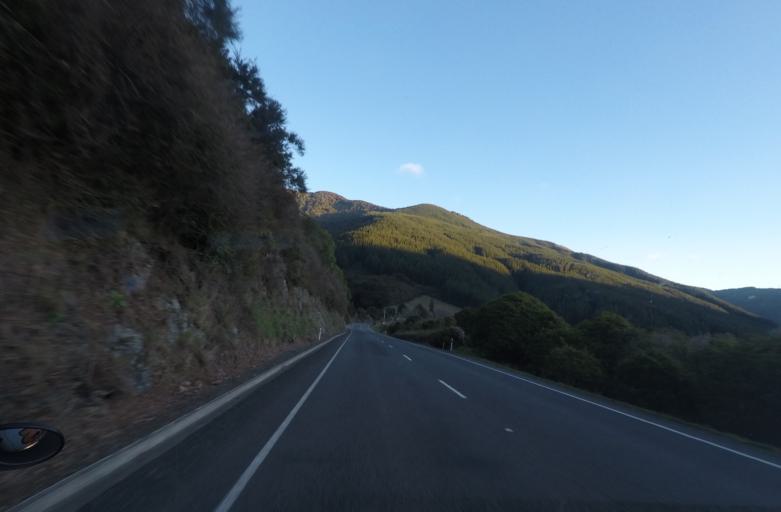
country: NZ
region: Marlborough
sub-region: Marlborough District
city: Picton
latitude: -41.2791
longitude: 173.7280
